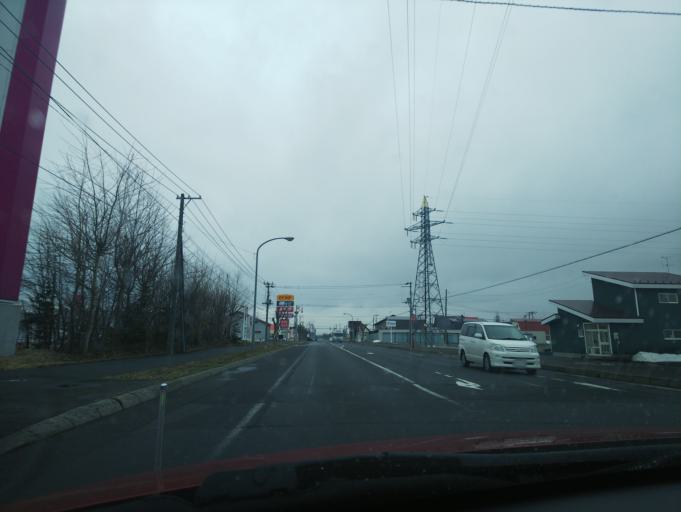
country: JP
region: Hokkaido
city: Nayoro
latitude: 44.3382
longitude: 142.4503
